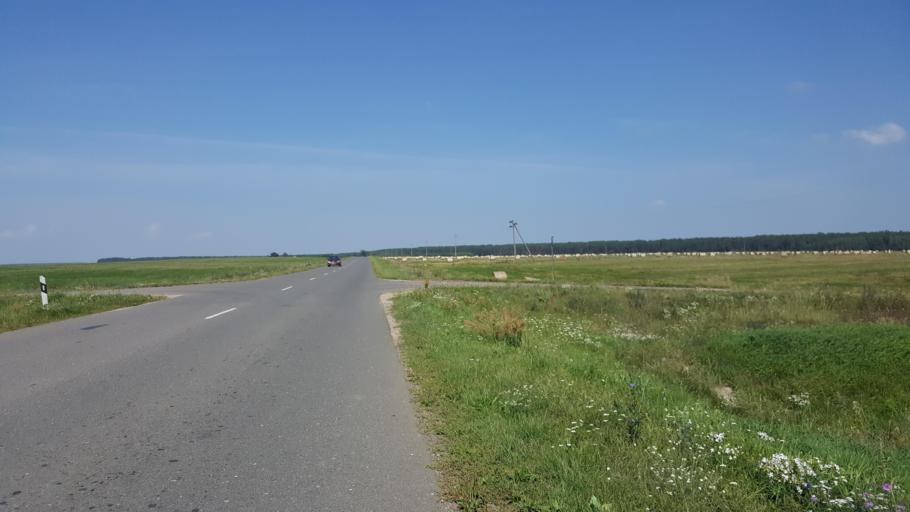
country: BY
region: Brest
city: Kamyanyuki
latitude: 52.4934
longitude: 23.6802
